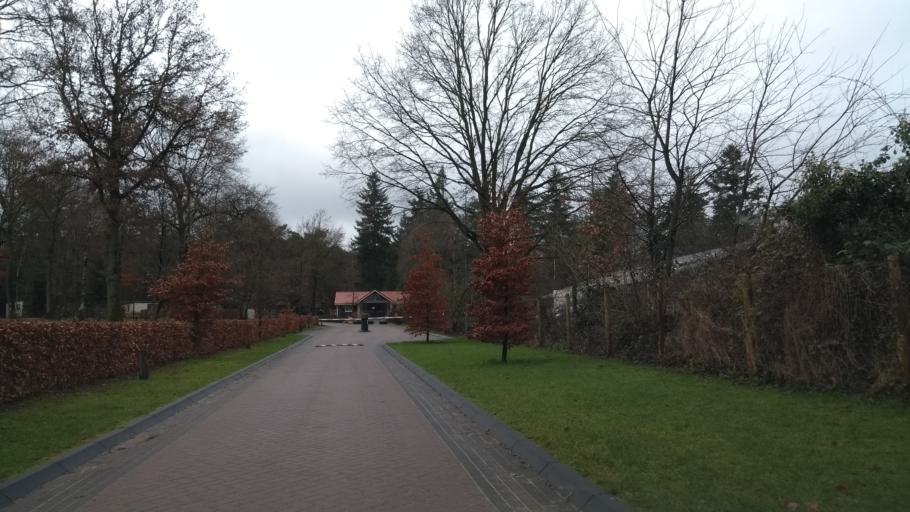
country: NL
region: Gelderland
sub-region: Gemeente Rheden
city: Dieren
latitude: 52.0684
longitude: 6.0804
